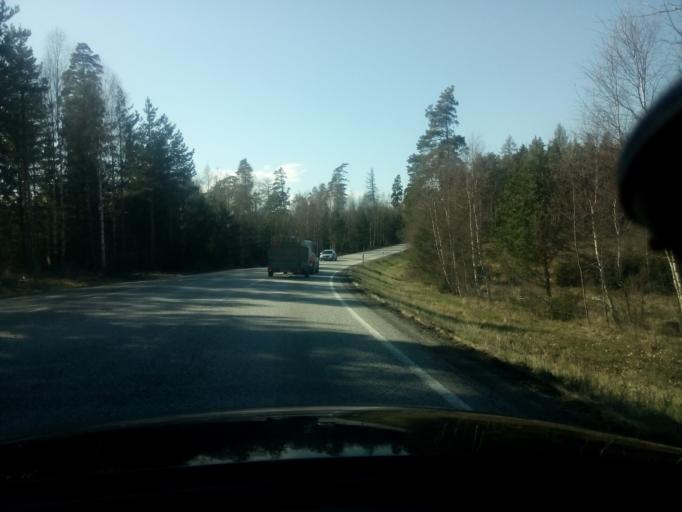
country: SE
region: Soedermanland
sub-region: Nykopings Kommun
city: Stigtomta
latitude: 58.8848
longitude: 16.8462
